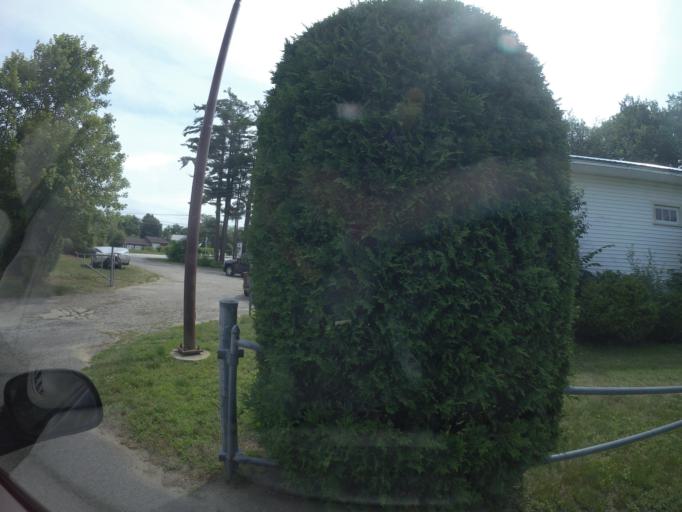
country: US
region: Maine
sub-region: Cumberland County
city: West Scarborough
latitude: 43.5509
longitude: -70.4088
